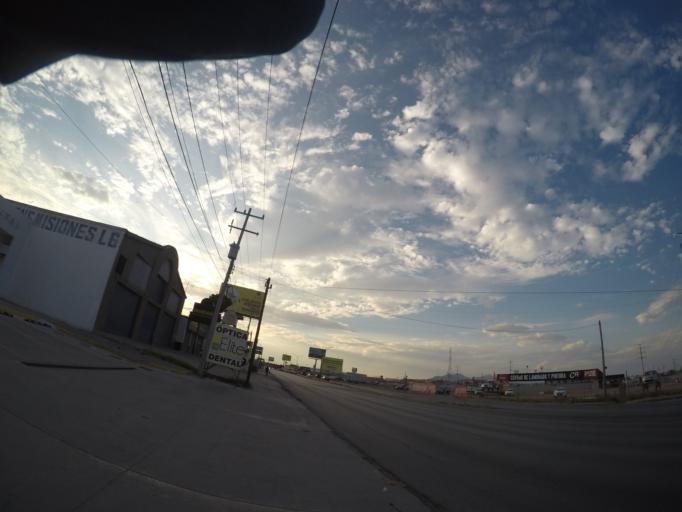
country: MX
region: Chihuahua
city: Ciudad Juarez
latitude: 31.7037
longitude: -106.4198
